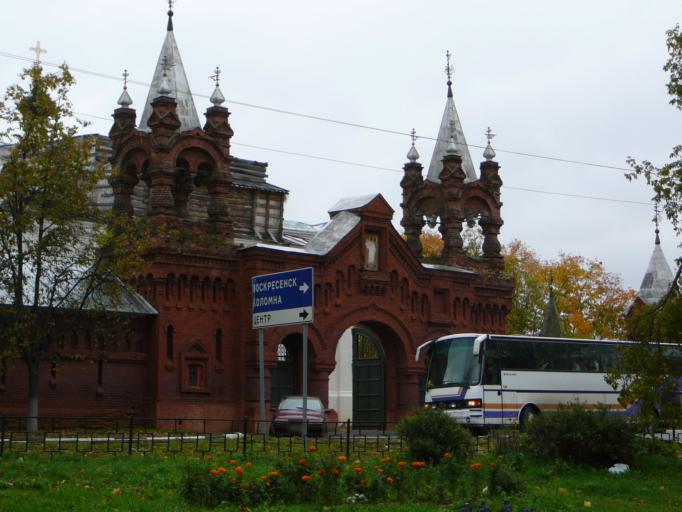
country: RU
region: Moskovskaya
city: Yegor'yevsk
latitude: 55.3884
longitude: 39.0299
